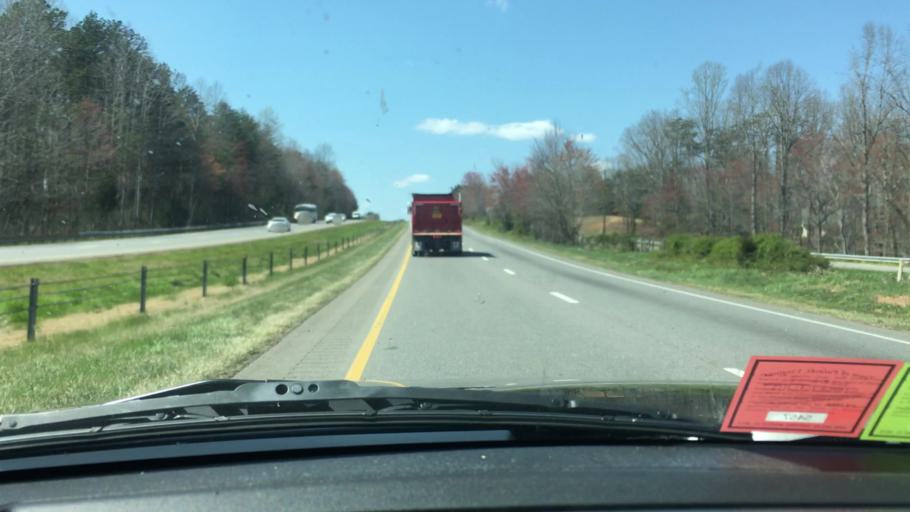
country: US
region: North Carolina
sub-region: Surry County
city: Pilot Mountain
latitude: 36.4259
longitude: -80.5204
